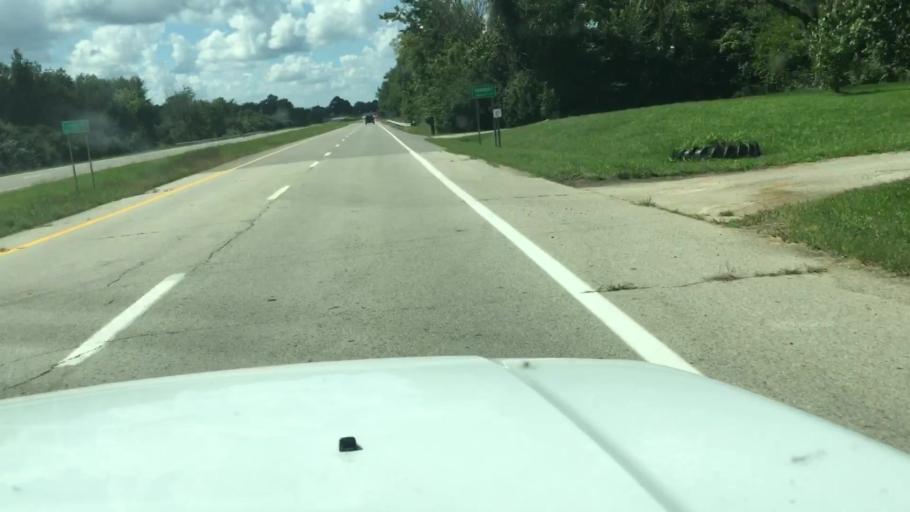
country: US
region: Ohio
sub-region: Madison County
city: Choctaw Lake
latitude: 39.9315
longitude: -83.5380
